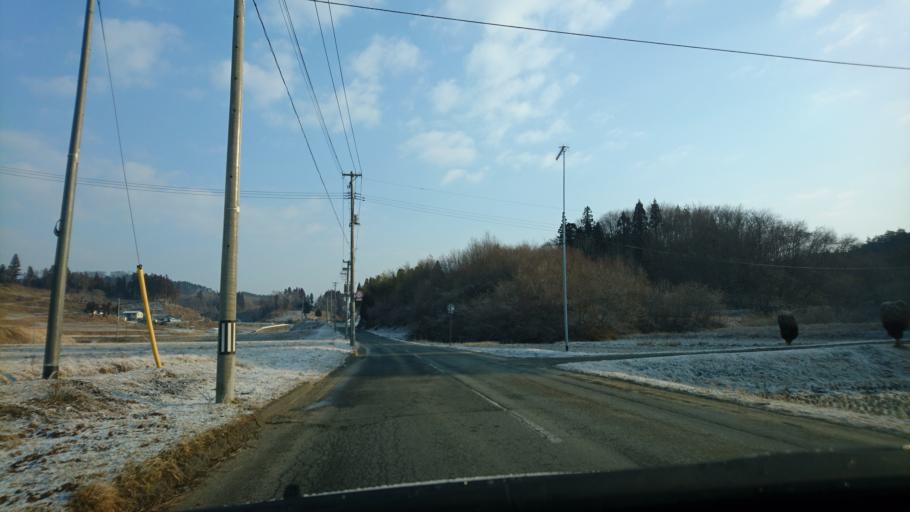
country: JP
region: Iwate
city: Ichinoseki
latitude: 38.9079
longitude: 141.3768
